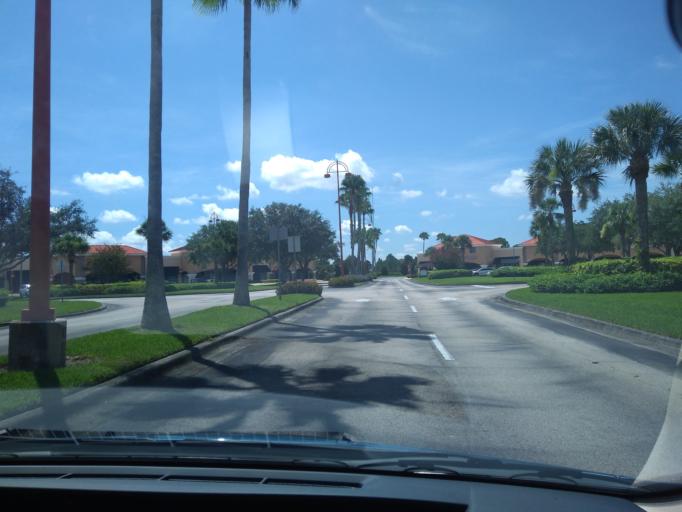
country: US
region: Florida
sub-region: Indian River County
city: West Vero Corridor
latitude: 27.6356
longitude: -80.5216
